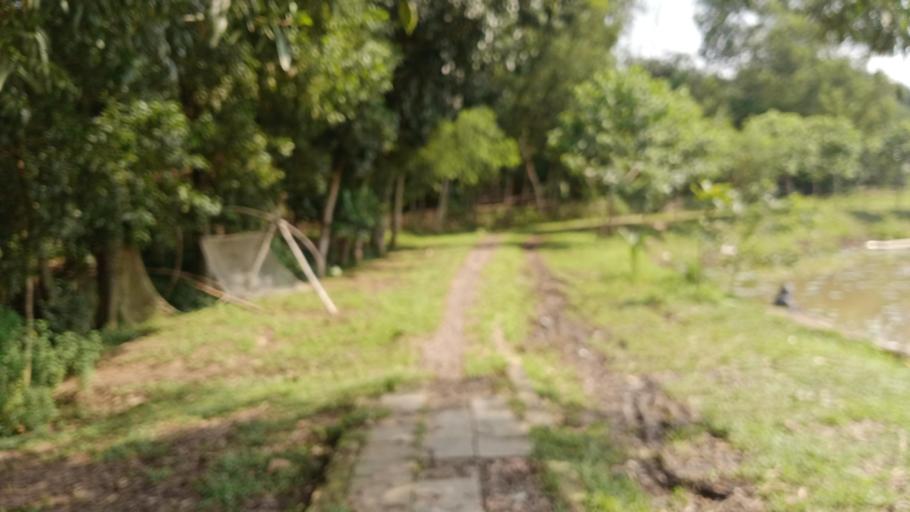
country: ID
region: West Java
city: Cileungsir
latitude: -6.3975
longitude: 107.0829
